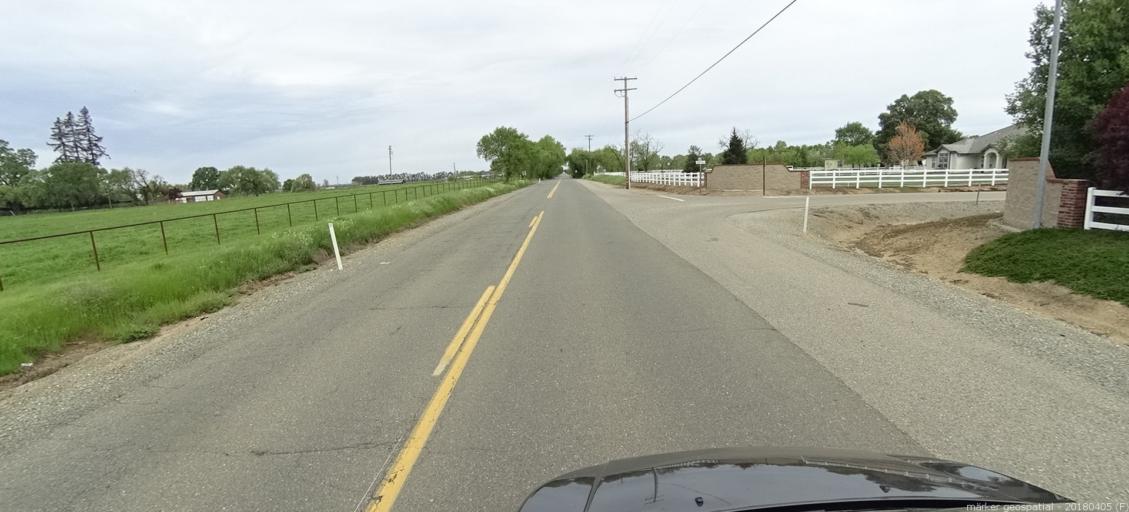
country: US
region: California
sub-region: Sacramento County
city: Galt
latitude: 38.2751
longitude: -121.3372
